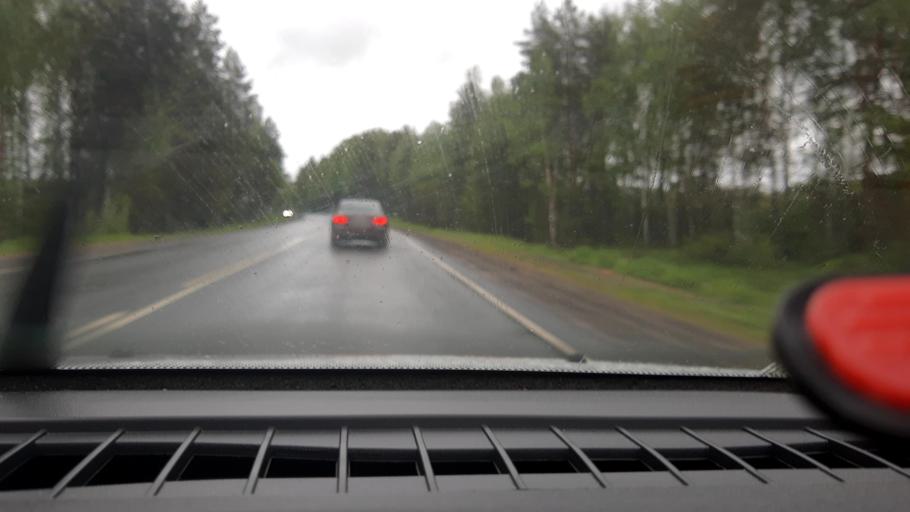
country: RU
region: Nizjnij Novgorod
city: Semenov
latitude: 56.7352
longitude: 44.3194
